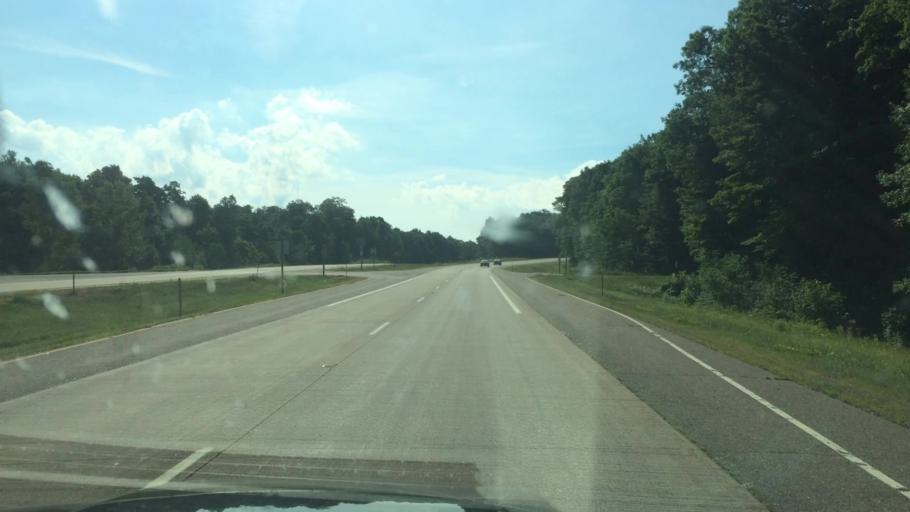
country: US
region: Wisconsin
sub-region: Shawano County
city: Wittenberg
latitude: 44.8246
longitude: -89.0640
